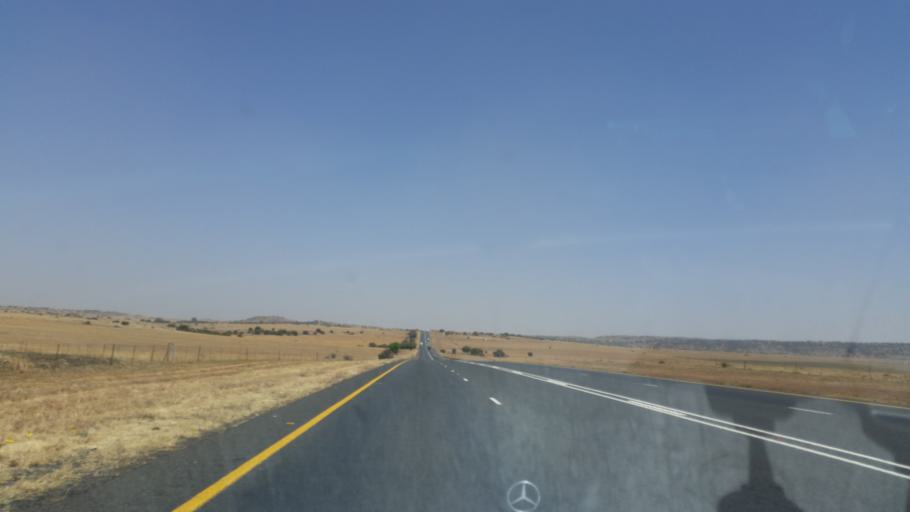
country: ZA
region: Orange Free State
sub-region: Lejweleputswa District Municipality
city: Winburg
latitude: -28.6827
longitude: 26.8268
